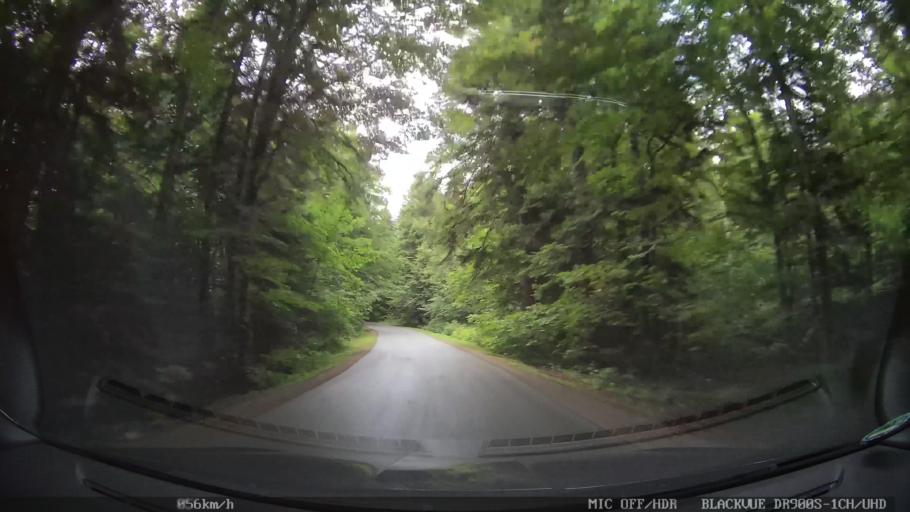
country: HR
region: Licko-Senjska
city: Jezerce
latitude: 44.9405
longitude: 15.5442
